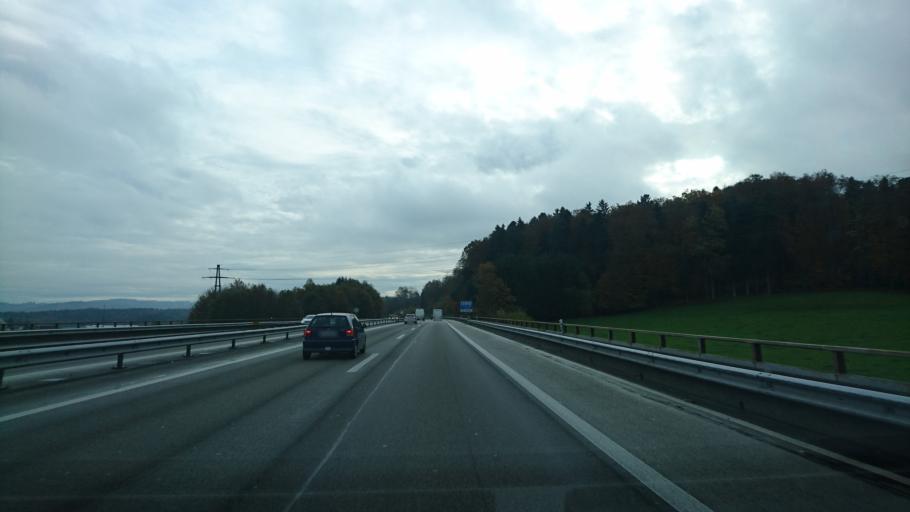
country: CH
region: Aargau
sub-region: Bezirk Zofingen
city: Safenwil
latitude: 47.3230
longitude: 8.0060
